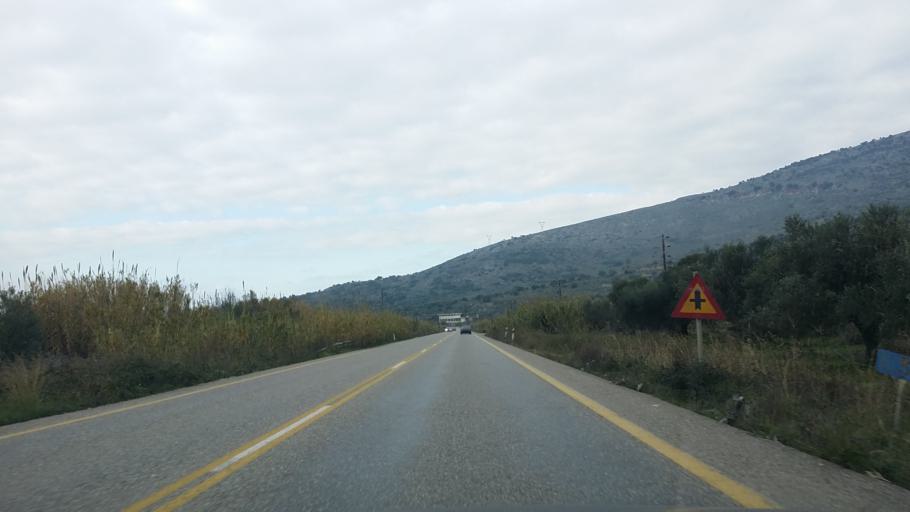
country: GR
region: West Greece
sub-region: Nomos Aitolias kai Akarnanias
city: Mesolongi
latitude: 38.4050
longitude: 21.4029
